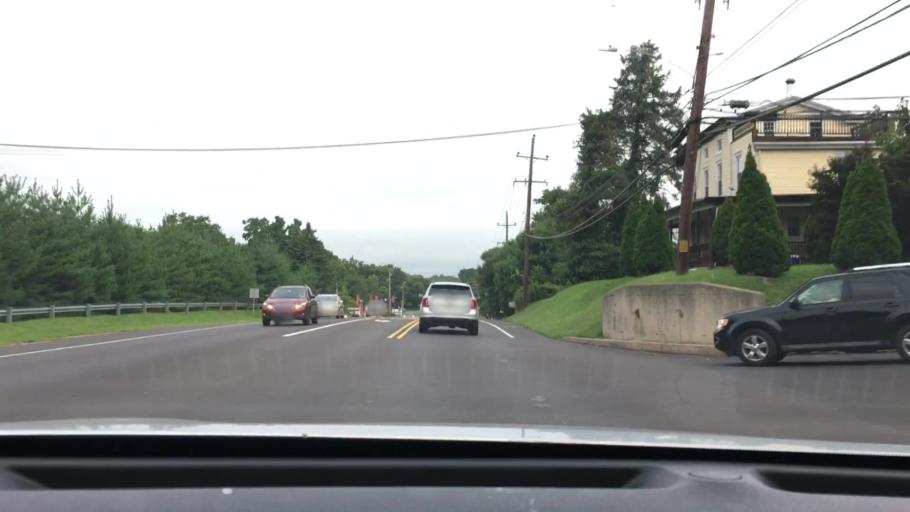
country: US
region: Pennsylvania
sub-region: Bucks County
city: Warminster Heights
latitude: 40.1650
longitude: -75.0605
